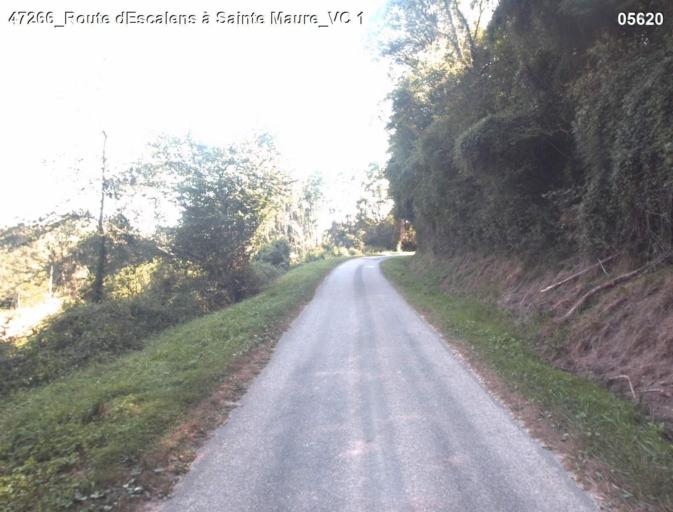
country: FR
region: Midi-Pyrenees
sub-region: Departement du Gers
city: Montreal
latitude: 44.0145
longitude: 0.1226
